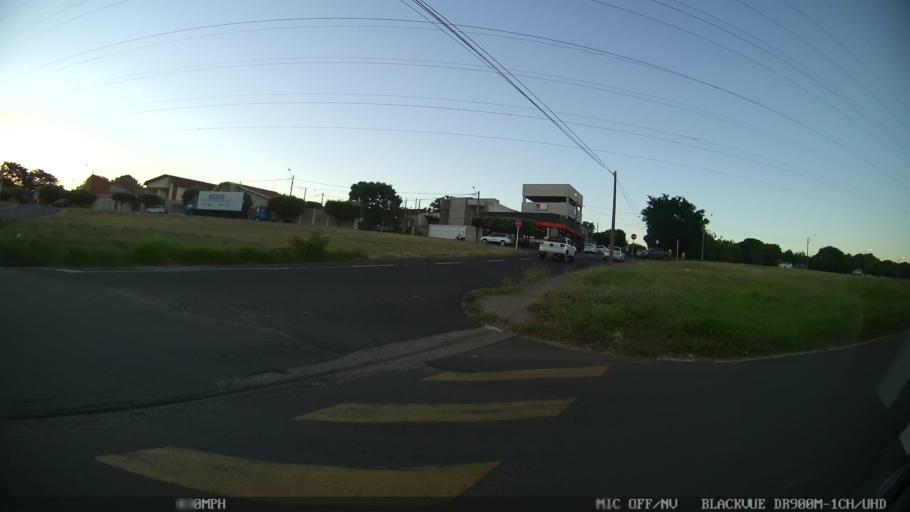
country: BR
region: Sao Paulo
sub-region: Sao Jose Do Rio Preto
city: Sao Jose do Rio Preto
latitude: -20.8443
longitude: -49.3823
